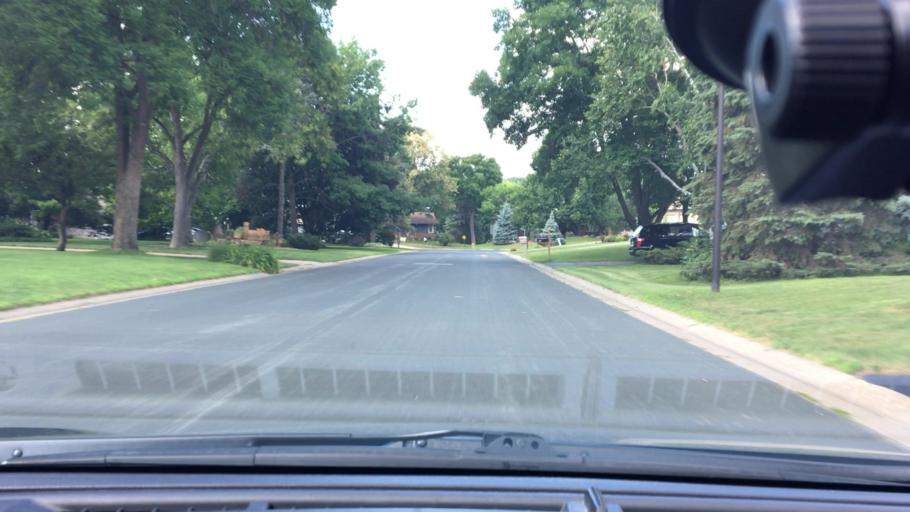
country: US
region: Minnesota
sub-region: Hennepin County
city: Plymouth
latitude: 45.0379
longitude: -93.4310
